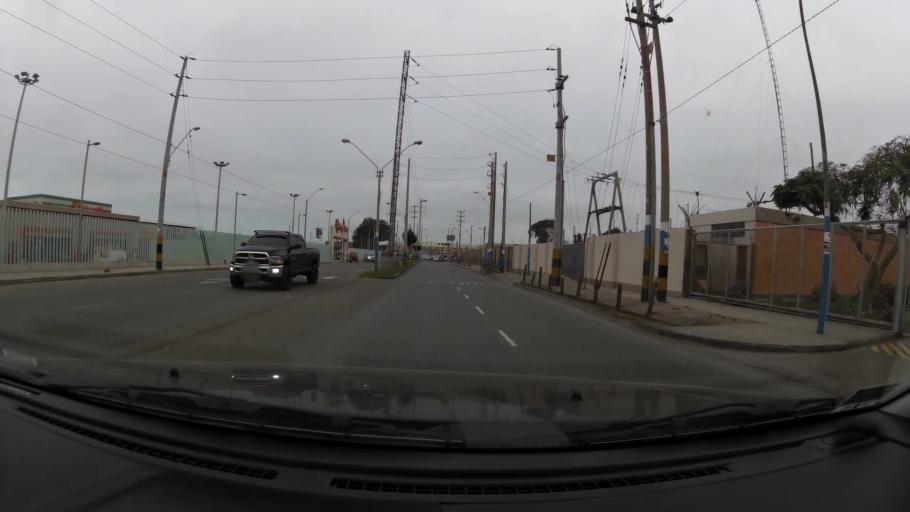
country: PE
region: Ica
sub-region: Provincia de Pisco
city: Pisco
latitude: -13.7125
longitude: -76.1944
